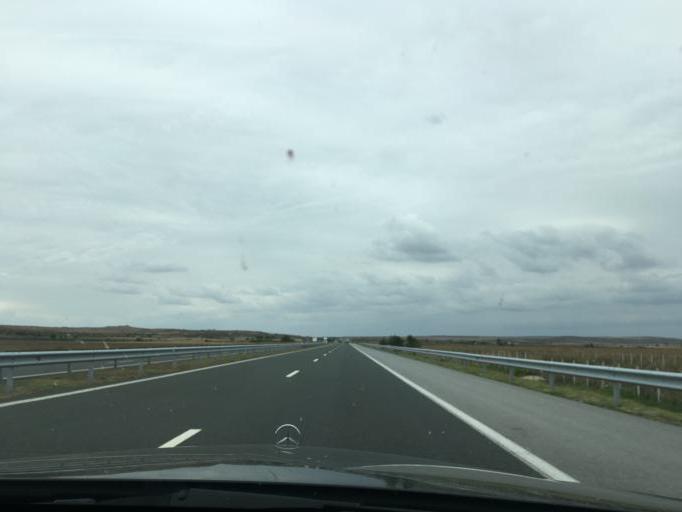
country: BG
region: Sliven
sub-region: Obshtina Sliven
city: Kermen
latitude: 42.5058
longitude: 26.3222
